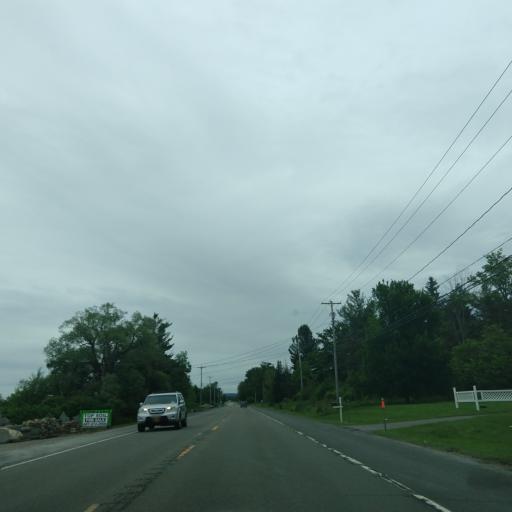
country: US
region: New York
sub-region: Tompkins County
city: Dryden
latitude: 42.4826
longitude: -76.3652
